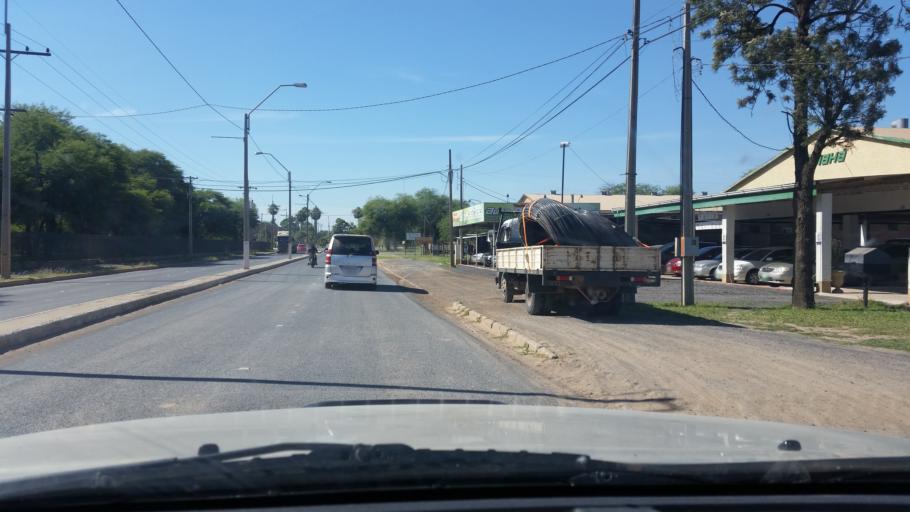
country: PY
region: Boqueron
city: Colonia Menno
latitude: -22.3757
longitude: -59.8372
